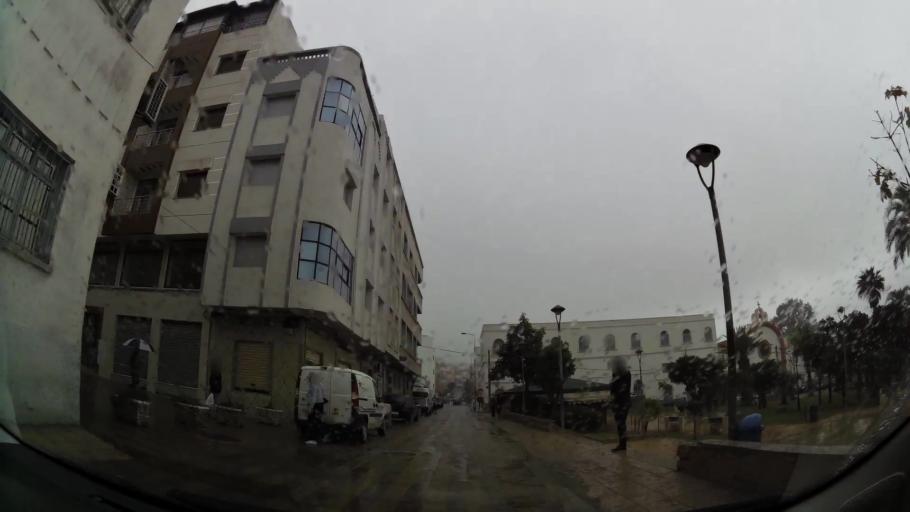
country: MA
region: Taza-Al Hoceima-Taounate
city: Al Hoceima
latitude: 35.2438
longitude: -3.9319
